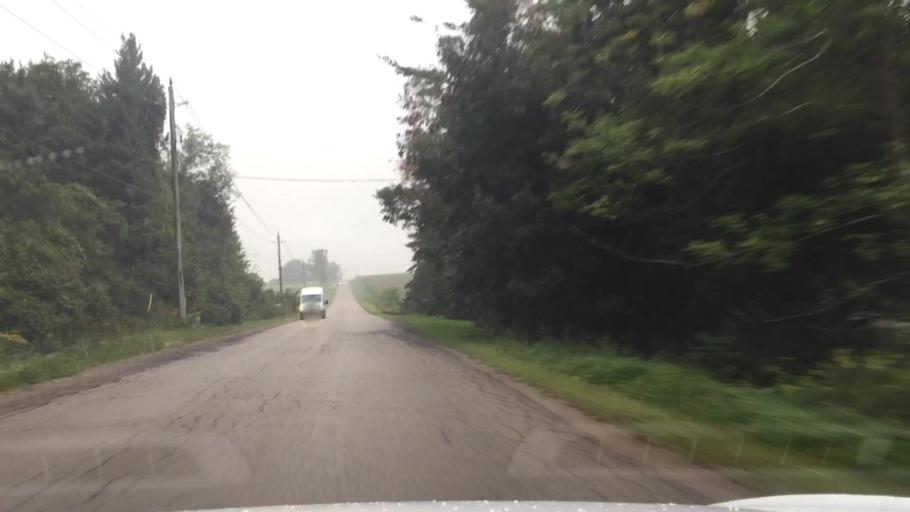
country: CA
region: Ontario
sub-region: Oxford County
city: Woodstock
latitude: 43.1136
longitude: -80.6957
